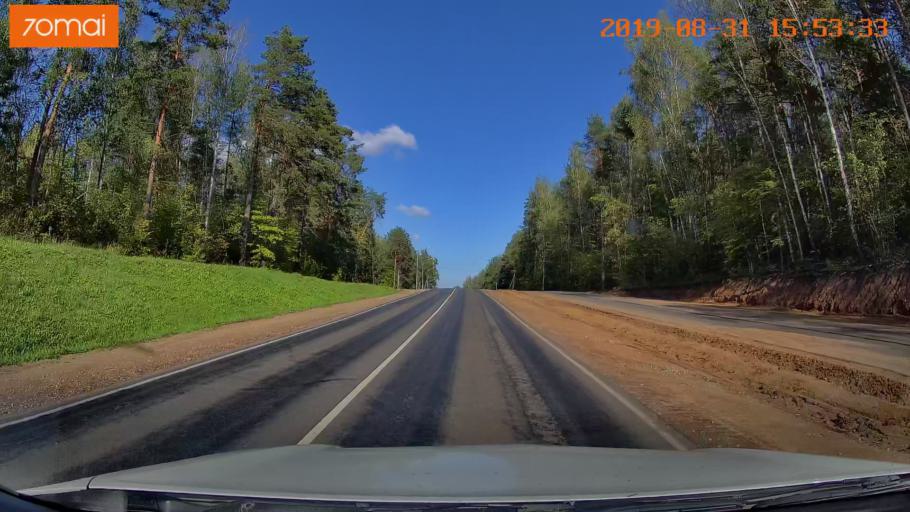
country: RU
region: Kaluga
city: Yukhnov
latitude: 54.7133
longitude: 35.1331
